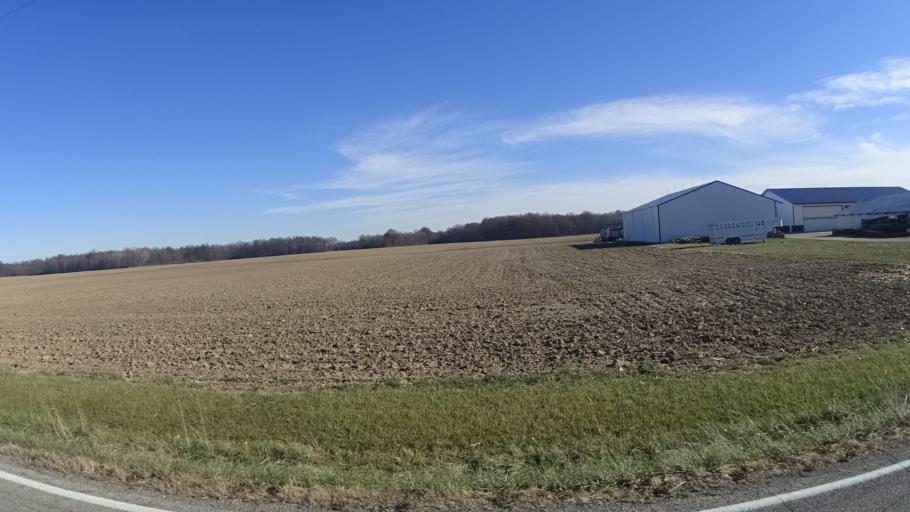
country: US
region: Ohio
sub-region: Lorain County
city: South Amherst
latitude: 41.3211
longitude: -82.2877
